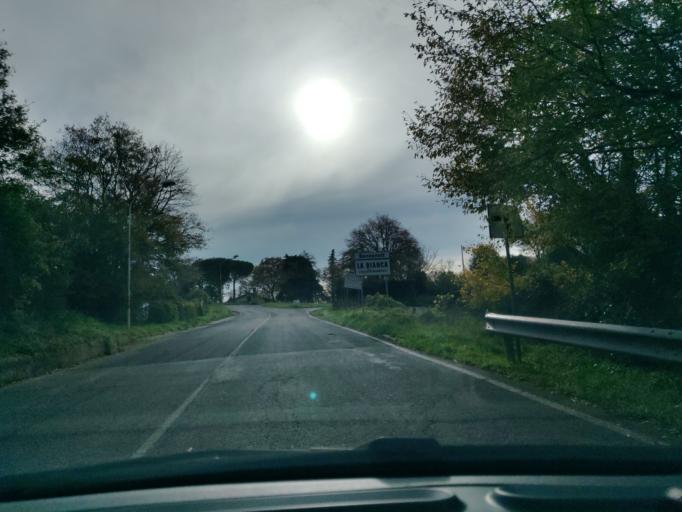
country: IT
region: Latium
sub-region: Citta metropolitana di Roma Capitale
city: Allumiere
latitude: 42.1488
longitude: 11.8991
